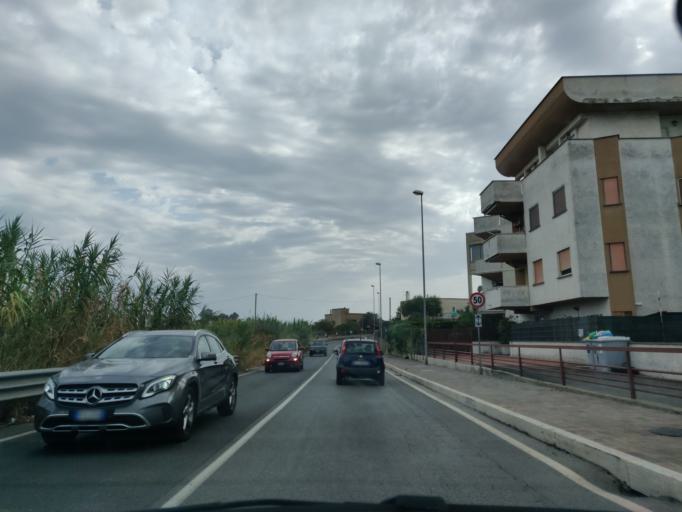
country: IT
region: Latium
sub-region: Citta metropolitana di Roma Capitale
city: Santa Marinella
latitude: 42.0399
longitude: 11.8816
